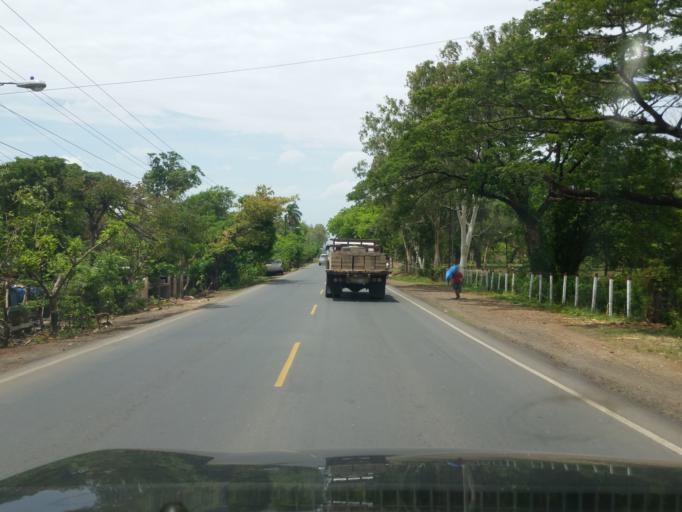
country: NI
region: Granada
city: Nandaime
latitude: 11.7735
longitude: -86.0520
